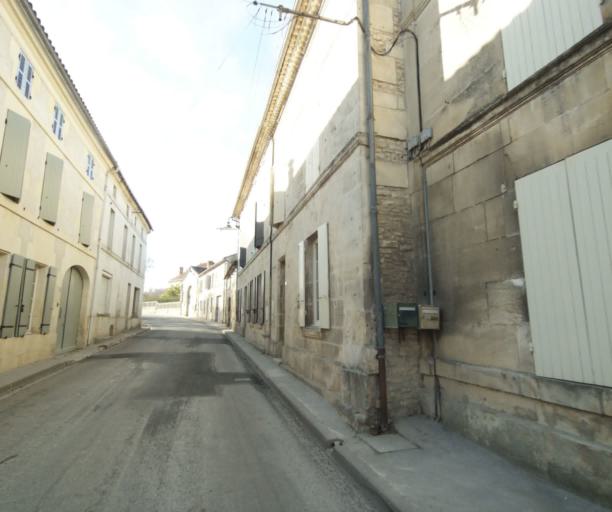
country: FR
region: Poitou-Charentes
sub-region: Departement de la Charente-Maritime
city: Burie
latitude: 45.7724
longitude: -0.4242
